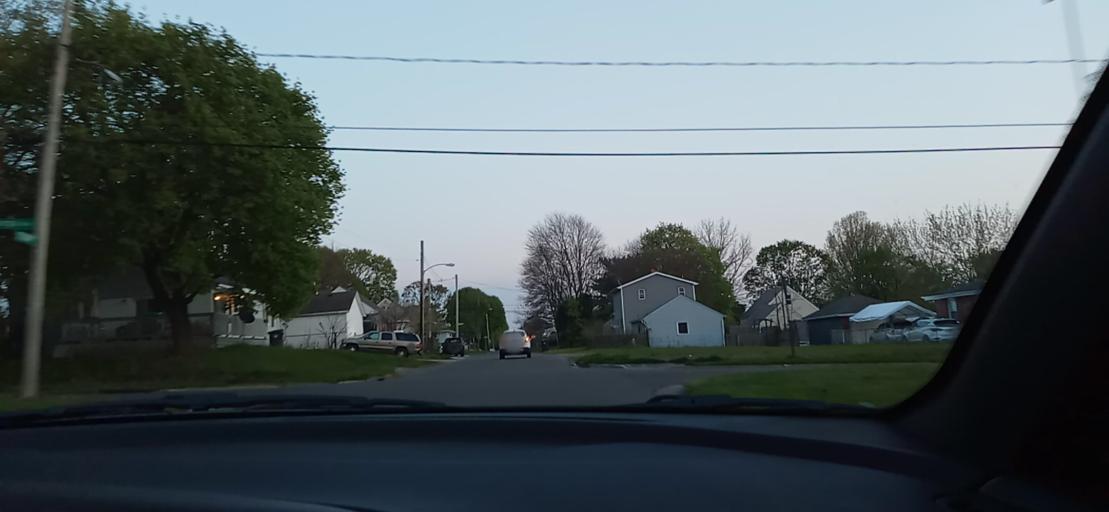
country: US
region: Ohio
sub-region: Summit County
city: Akron
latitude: 41.0440
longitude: -81.4943
